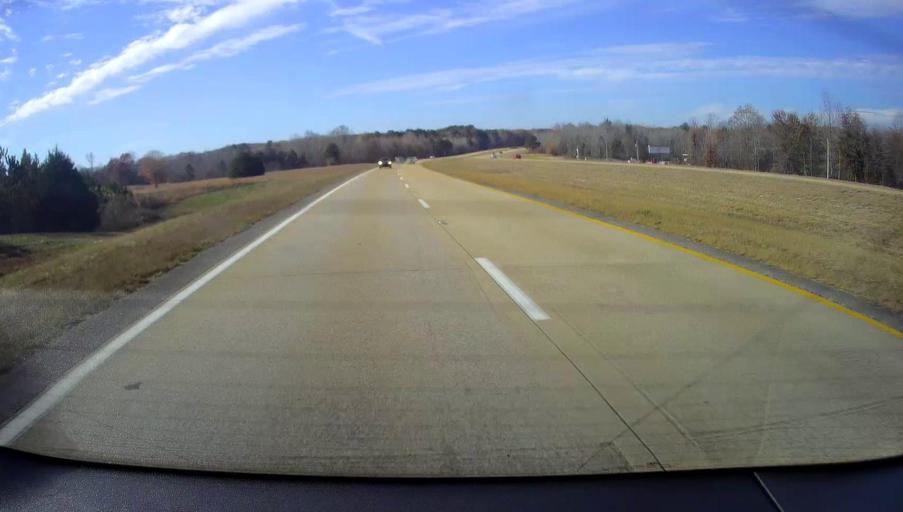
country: US
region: Mississippi
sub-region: Tishomingo County
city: Iuka
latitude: 34.8084
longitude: -88.2733
